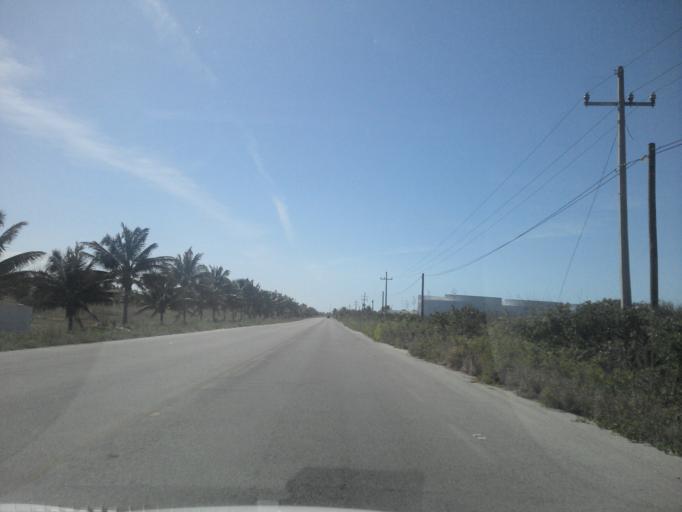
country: MX
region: Yucatan
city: Telchac Puerto
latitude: 21.3320
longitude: -89.3686
